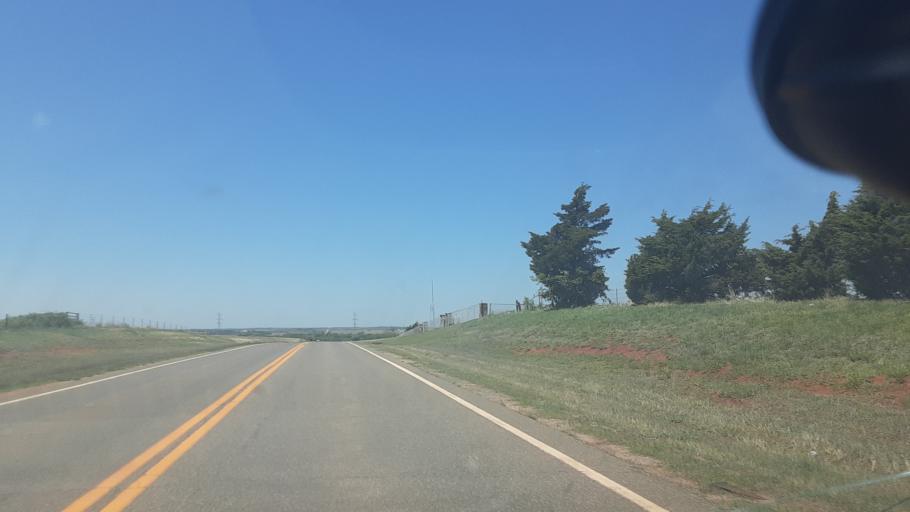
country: US
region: Oklahoma
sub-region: Noble County
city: Perry
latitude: 36.1157
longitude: -97.3621
